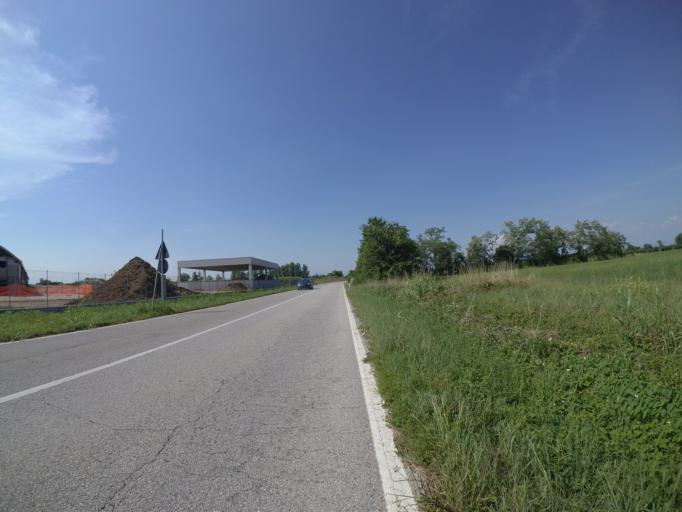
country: IT
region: Friuli Venezia Giulia
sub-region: Provincia di Udine
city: Talmassons
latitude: 45.9385
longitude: 13.1275
